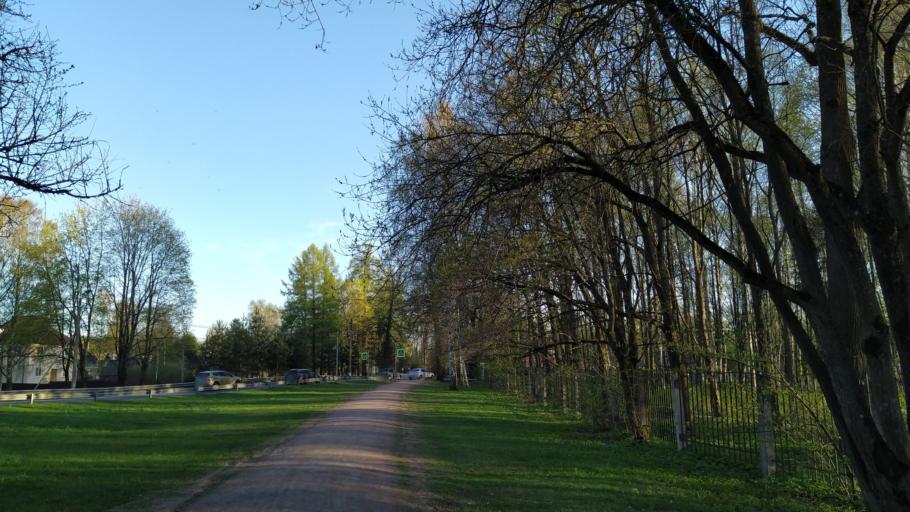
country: RU
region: St.-Petersburg
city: Pavlovsk
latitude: 59.6978
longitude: 30.4288
